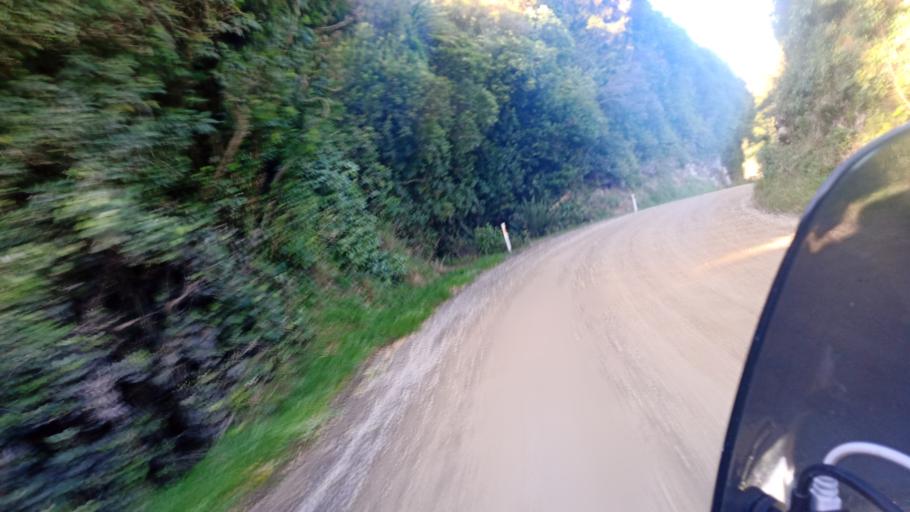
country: NZ
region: Hawke's Bay
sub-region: Wairoa District
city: Wairoa
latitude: -38.7944
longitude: 177.1251
